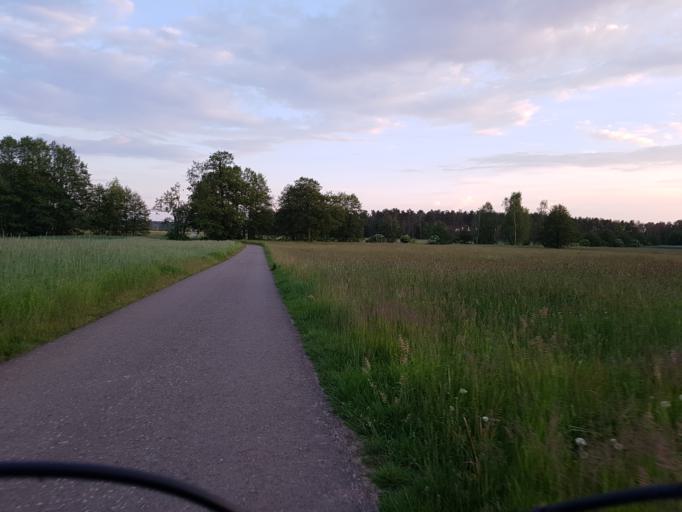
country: DE
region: Brandenburg
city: Bad Liebenwerda
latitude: 51.5538
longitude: 13.4162
